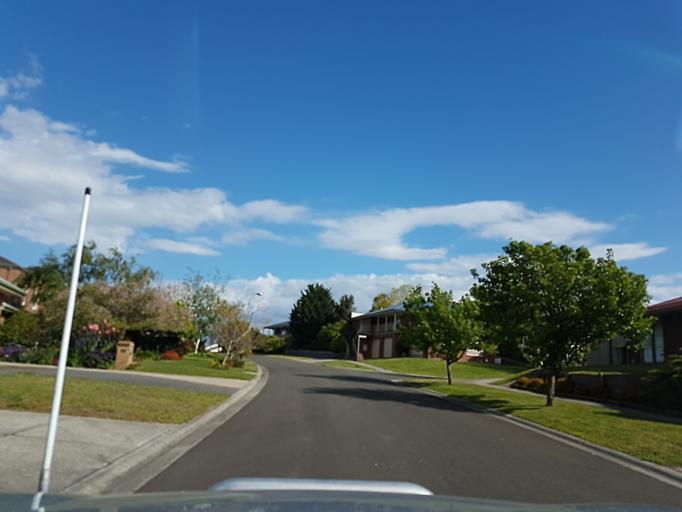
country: AU
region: Victoria
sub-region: Cardinia
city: Pakenham Upper
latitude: -38.0645
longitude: 145.4785
